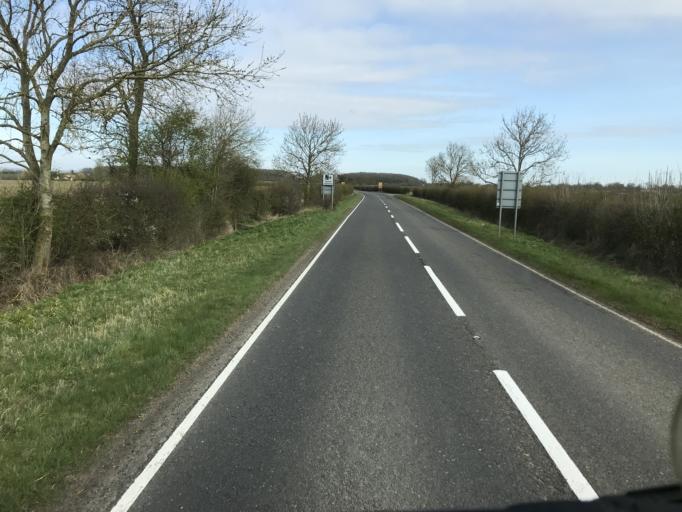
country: GB
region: England
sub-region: Lincolnshire
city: Market Rasen
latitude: 53.3964
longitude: -0.4185
